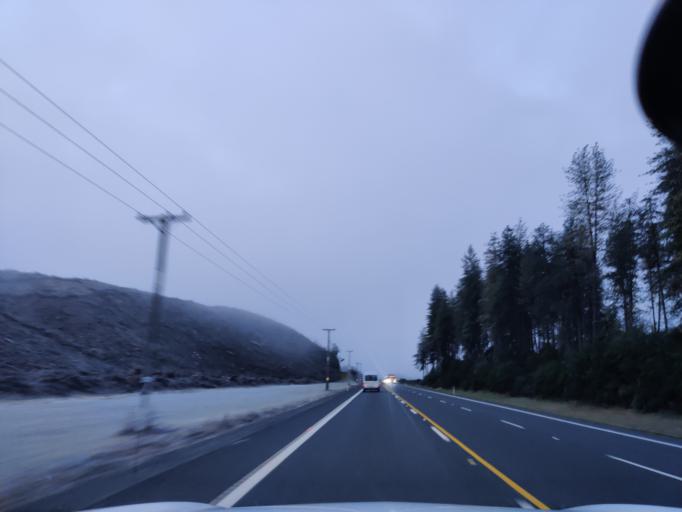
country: NZ
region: Waikato
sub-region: South Waikato District
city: Tokoroa
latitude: -38.3845
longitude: 176.0060
